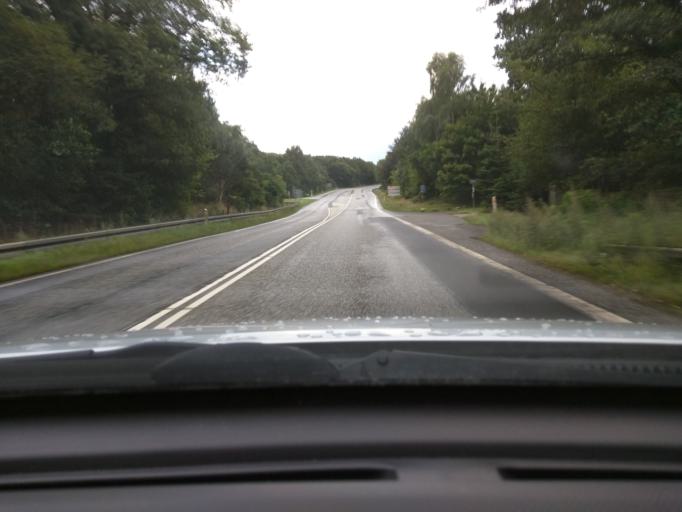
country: DK
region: Central Jutland
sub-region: Viborg Kommune
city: Viborg
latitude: 56.4007
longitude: 9.3724
